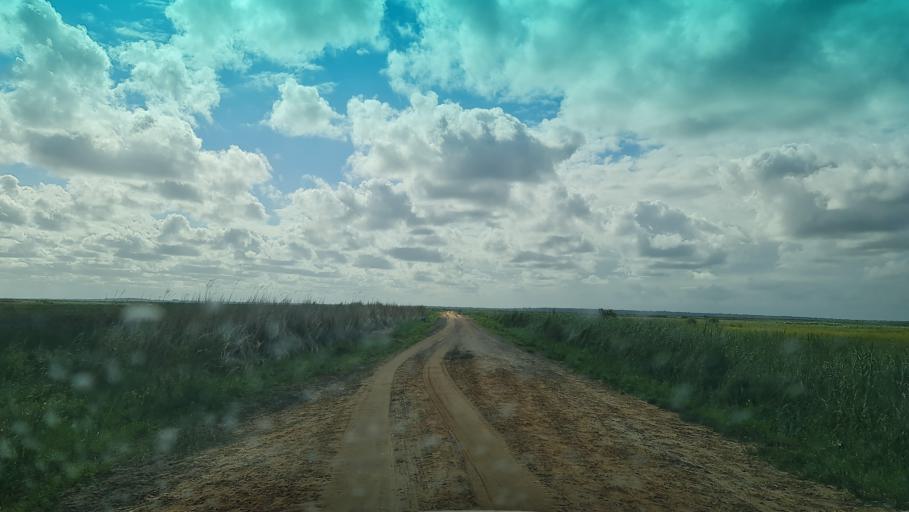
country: MZ
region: Maputo
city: Manhica
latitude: -25.4364
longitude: 32.8767
